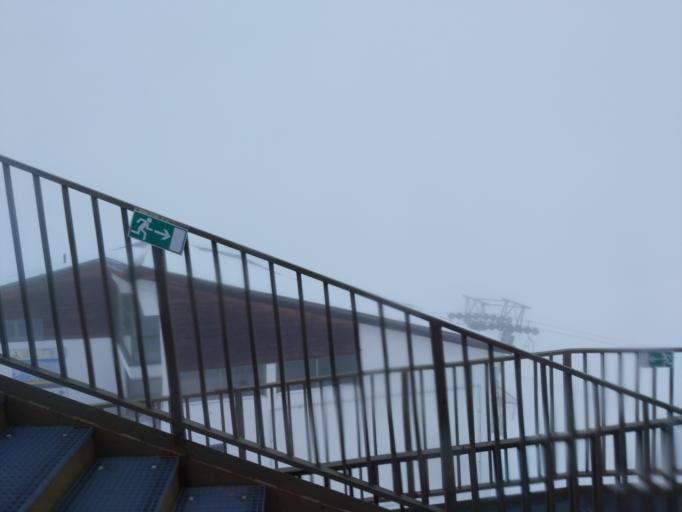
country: AT
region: Tyrol
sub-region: Politischer Bezirk Innsbruck Land
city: Axams
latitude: 47.1873
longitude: 11.2893
